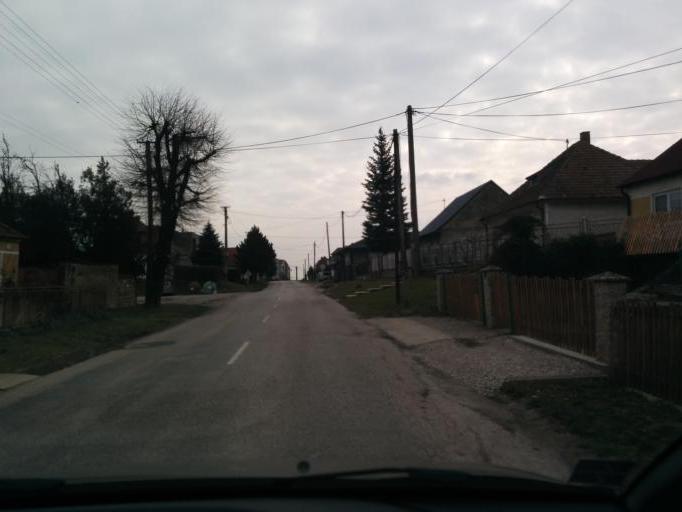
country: SK
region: Trnavsky
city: Sladkovicovo
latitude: 48.2801
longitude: 17.6302
